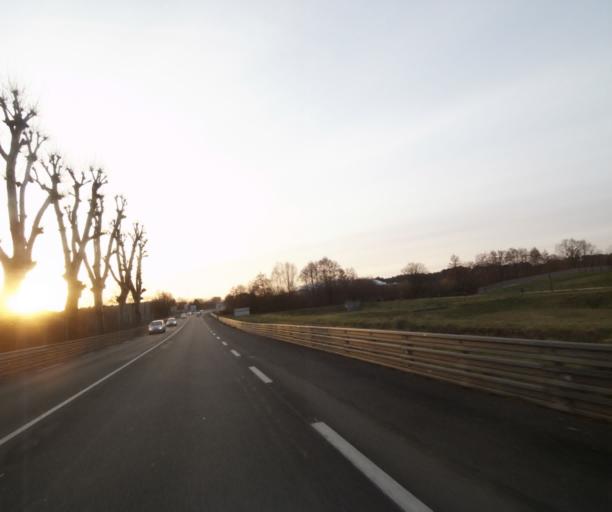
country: FR
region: Pays de la Loire
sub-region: Departement de la Sarthe
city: Ruaudin
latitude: 47.9595
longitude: 0.2253
